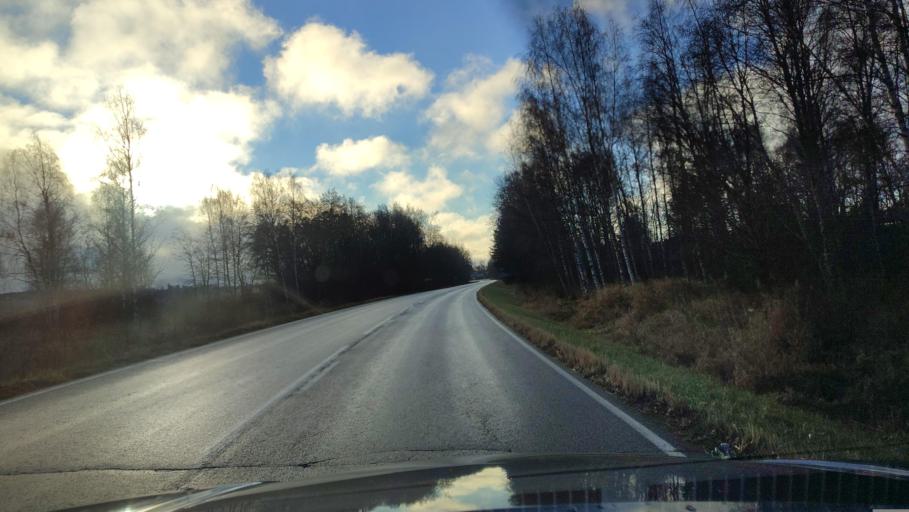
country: FI
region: Ostrobothnia
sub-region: Sydosterbotten
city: Kristinestad
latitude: 62.2852
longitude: 21.3781
